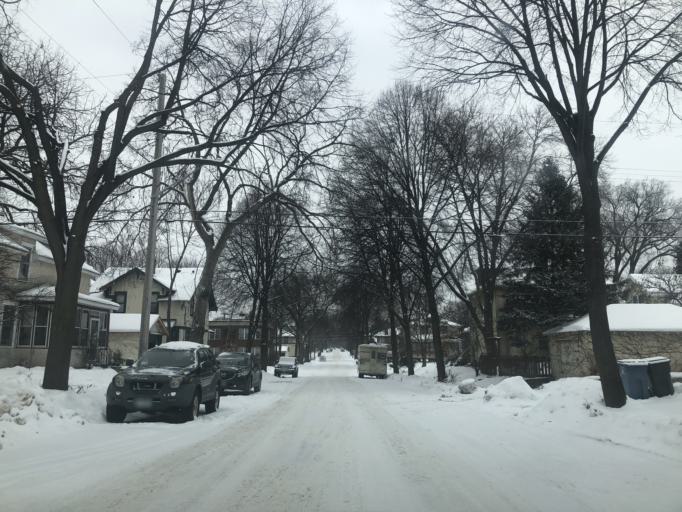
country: US
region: Minnesota
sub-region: Hennepin County
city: Richfield
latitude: 44.9287
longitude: -93.2822
